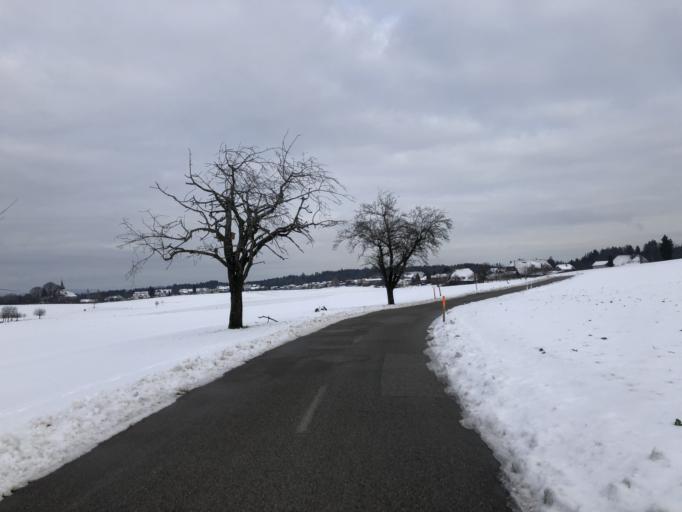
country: CH
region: Bern
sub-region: Oberaargau
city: Herzogenbuchsee
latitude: 47.1986
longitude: 7.7466
